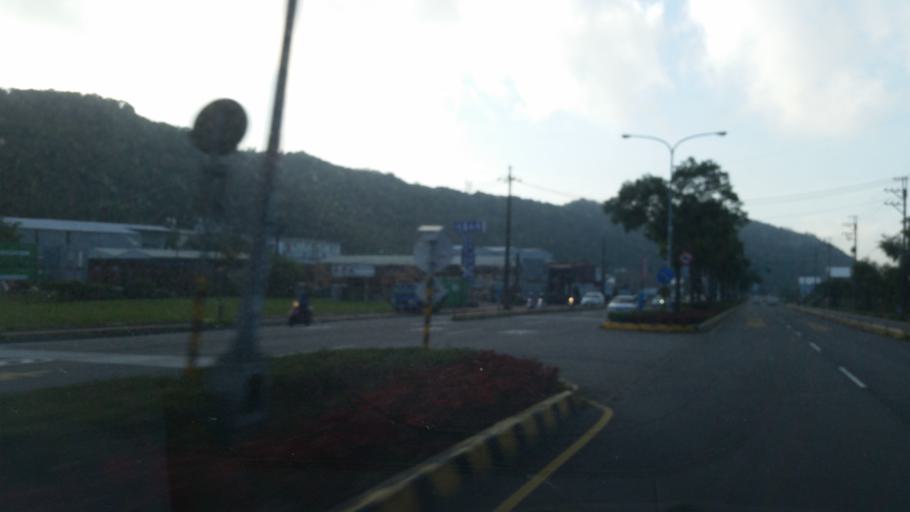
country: TW
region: Taiwan
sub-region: Taoyuan
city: Taoyuan
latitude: 25.0166
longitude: 121.3482
